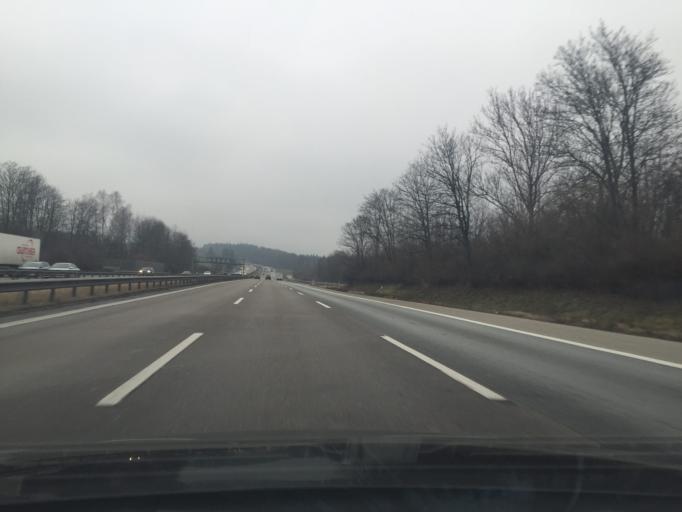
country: DE
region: Bavaria
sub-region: Upper Bavaria
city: Vagen
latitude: 47.8572
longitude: 11.8563
